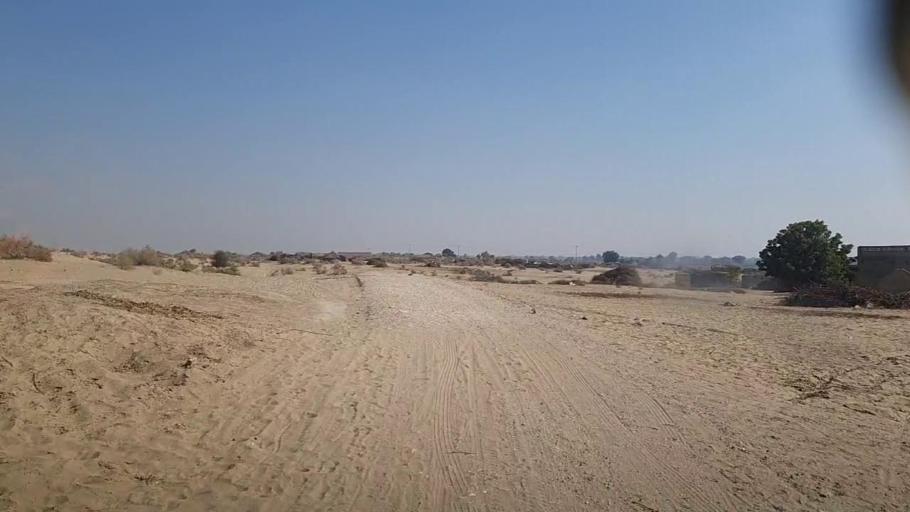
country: PK
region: Sindh
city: Khairpur
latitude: 28.0026
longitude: 69.8575
